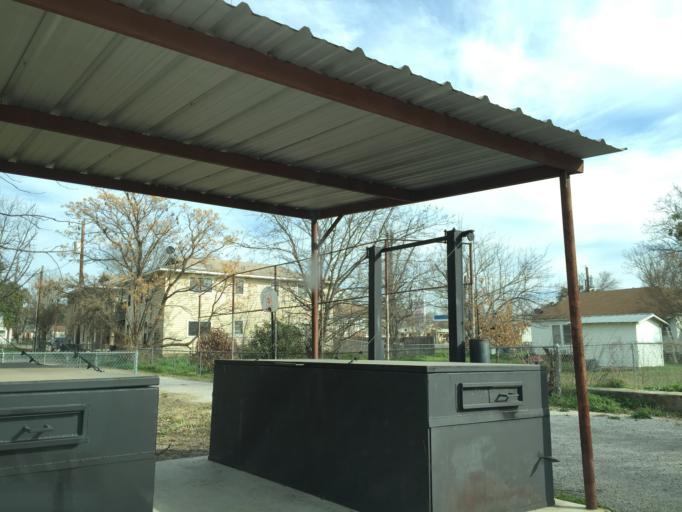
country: US
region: Texas
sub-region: Llano County
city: Llano
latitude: 30.7440
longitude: -98.6769
